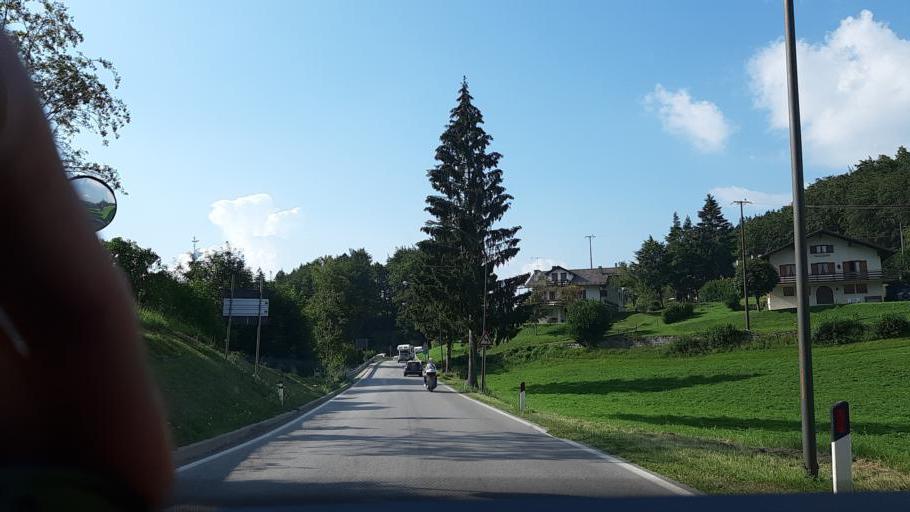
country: IT
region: Trentino-Alto Adige
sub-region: Provincia di Trento
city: Centa San Nicolo
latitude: 45.9461
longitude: 11.2476
